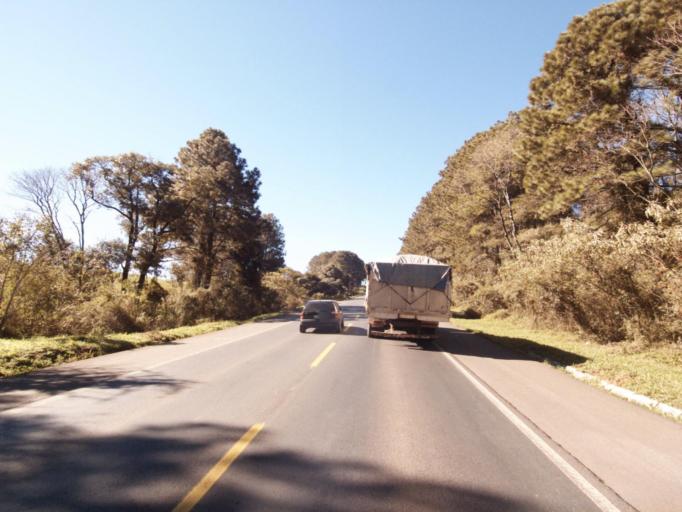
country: BR
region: Santa Catarina
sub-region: Xanxere
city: Xanxere
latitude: -26.9108
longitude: -52.4721
